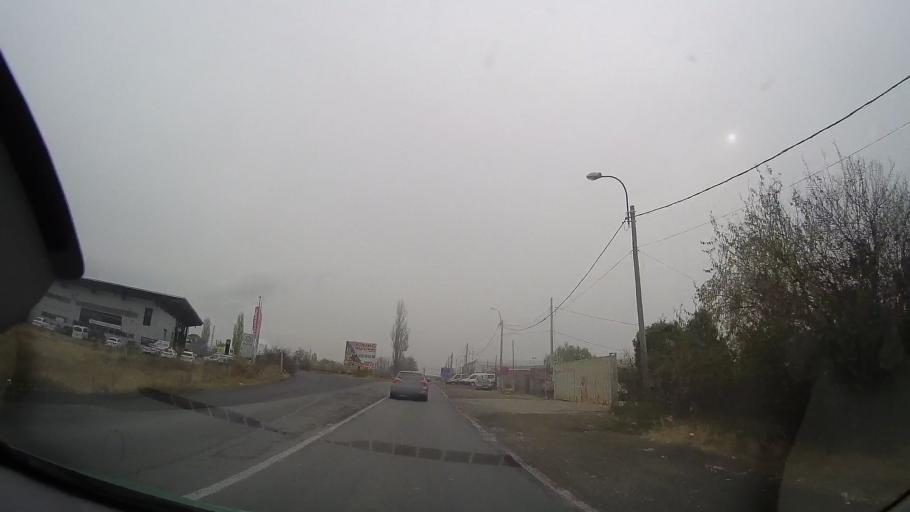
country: RO
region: Prahova
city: Ploiesti
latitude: 44.9581
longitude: 26.0479
